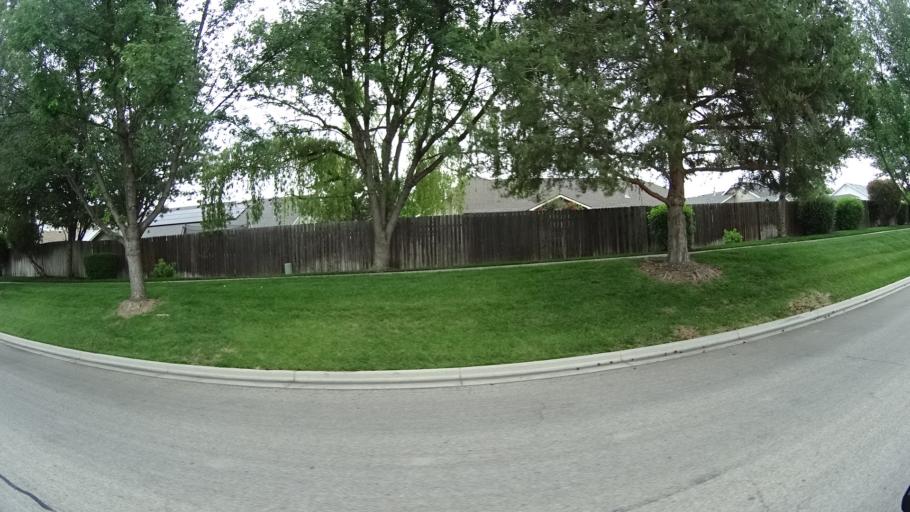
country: US
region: Idaho
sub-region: Ada County
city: Meridian
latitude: 43.5850
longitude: -116.3303
